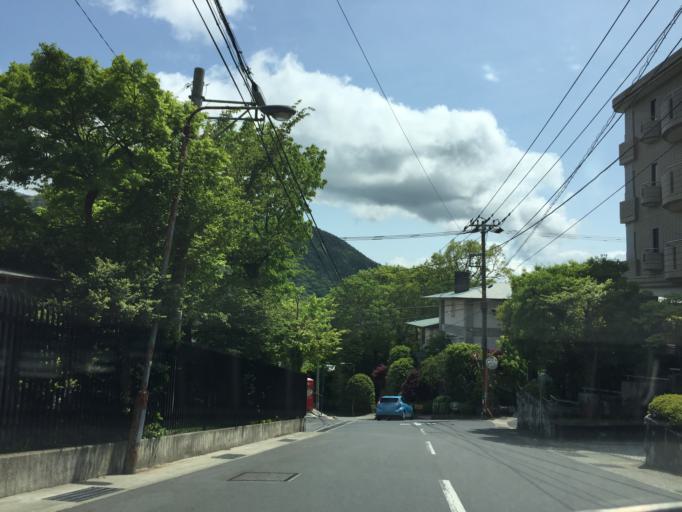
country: JP
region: Kanagawa
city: Hakone
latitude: 35.2482
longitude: 139.0459
